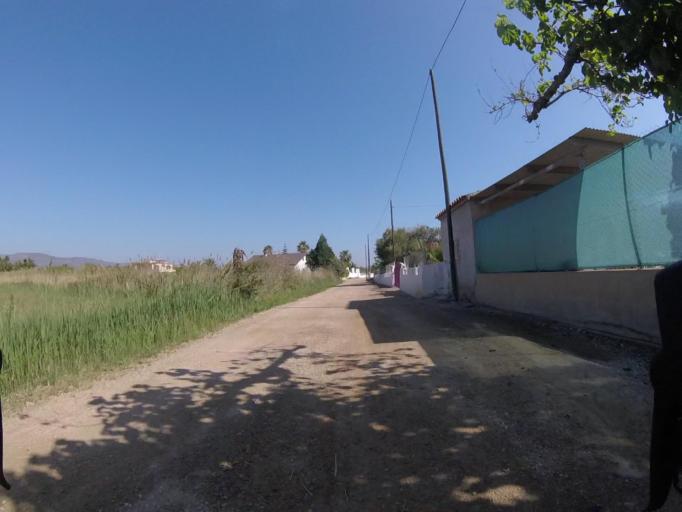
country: ES
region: Valencia
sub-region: Provincia de Castello
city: Orpesa/Oropesa del Mar
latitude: 40.1479
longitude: 0.1655
